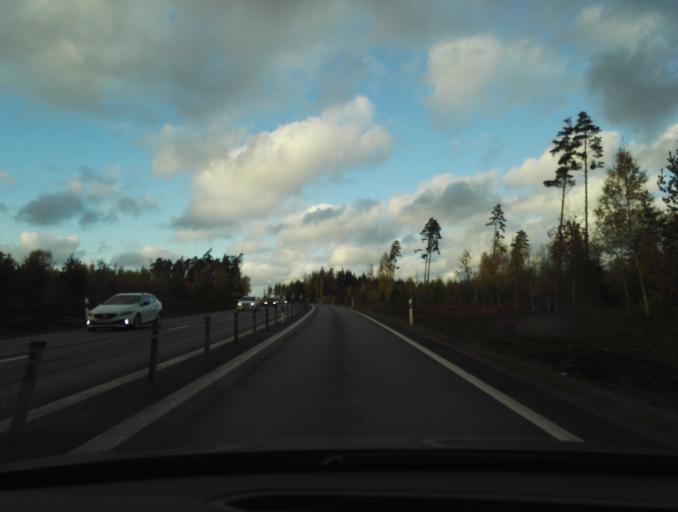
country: SE
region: Kronoberg
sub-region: Vaxjo Kommun
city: Vaexjoe
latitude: 56.9036
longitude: 14.7291
